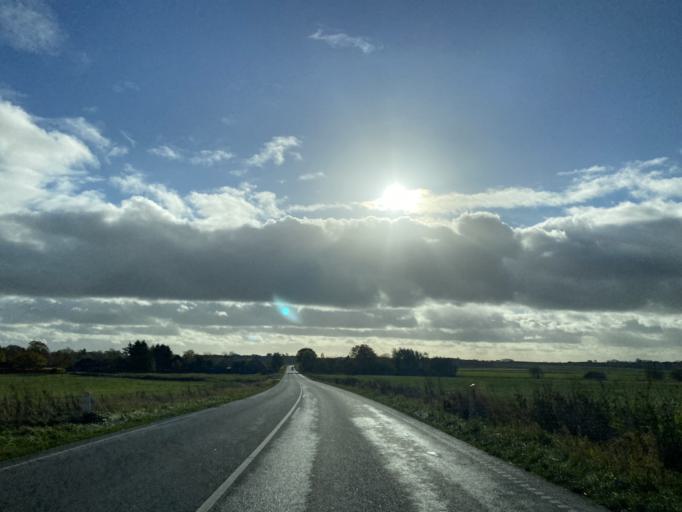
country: DK
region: Central Jutland
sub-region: Viborg Kommune
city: Bjerringbro
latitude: 56.3436
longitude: 9.6803
